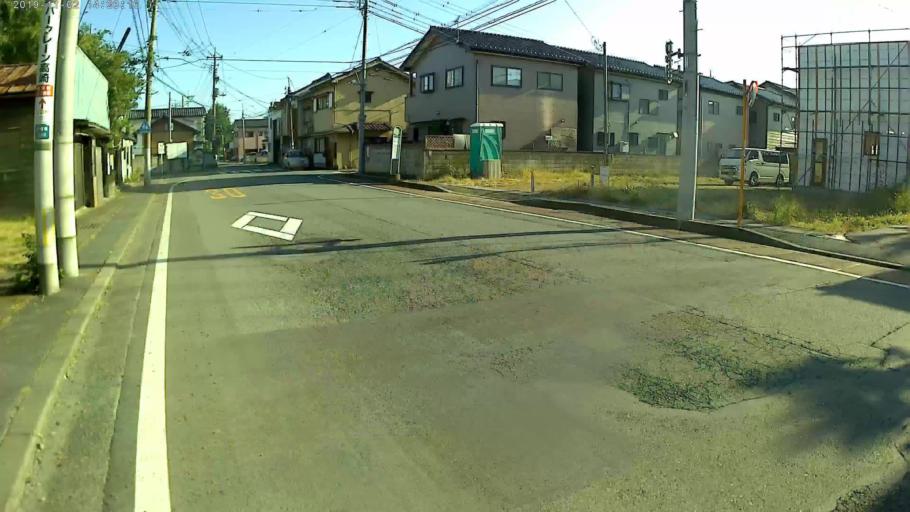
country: JP
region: Gunma
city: Takasaki
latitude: 36.3324
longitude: 138.9933
